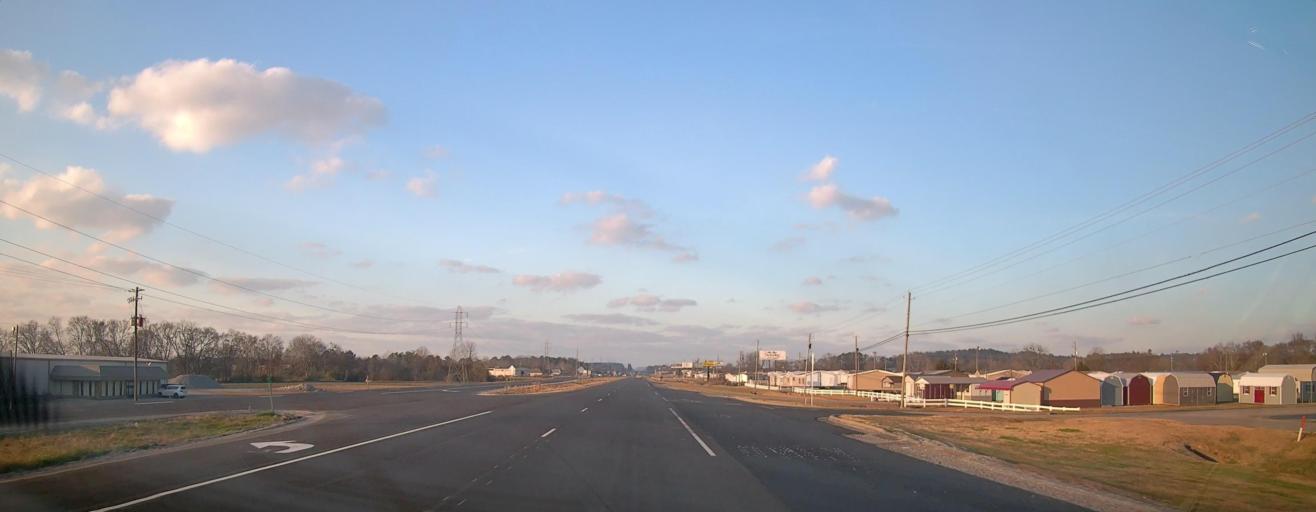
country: US
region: Alabama
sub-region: Calhoun County
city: Alexandria
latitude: 33.7695
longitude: -85.8930
